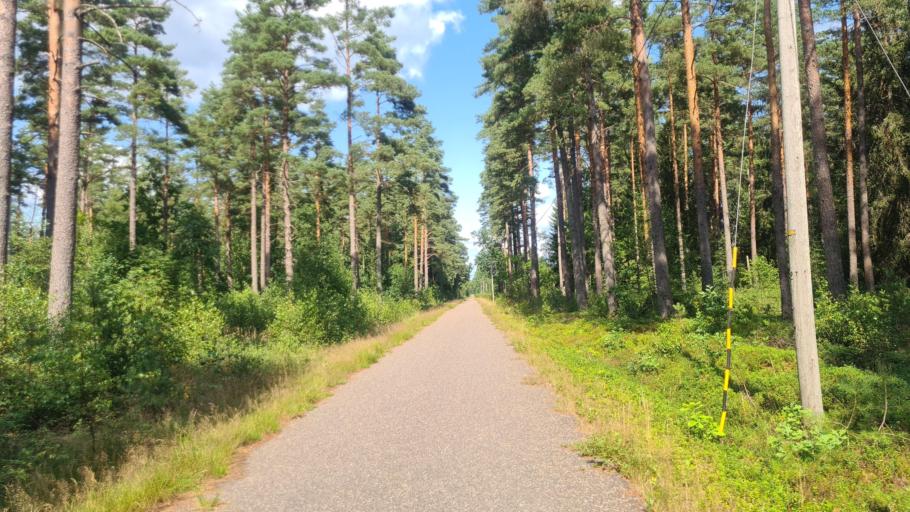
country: SE
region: Kronoberg
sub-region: Ljungby Kommun
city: Ljungby
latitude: 56.8453
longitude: 13.9636
